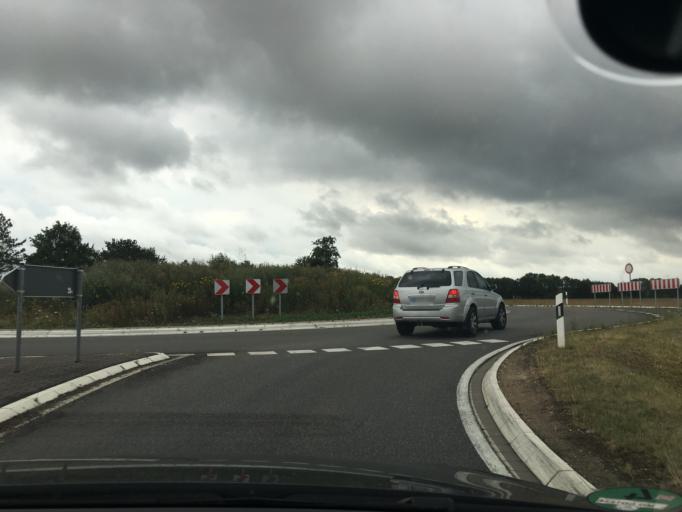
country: DE
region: North Rhine-Westphalia
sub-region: Regierungsbezirk Koln
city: Vettweiss
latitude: 50.7183
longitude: 6.5788
